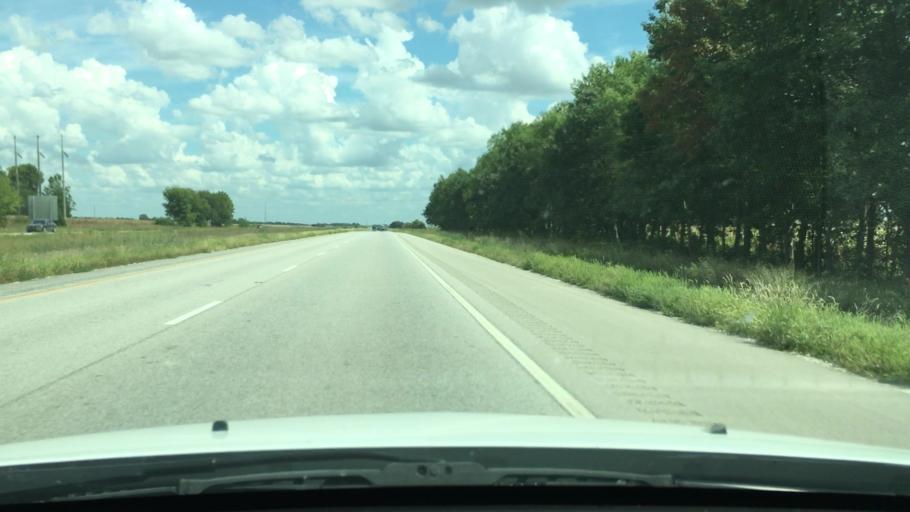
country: US
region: Illinois
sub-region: Sangamon County
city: New Berlin
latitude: 39.7368
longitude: -90.0175
